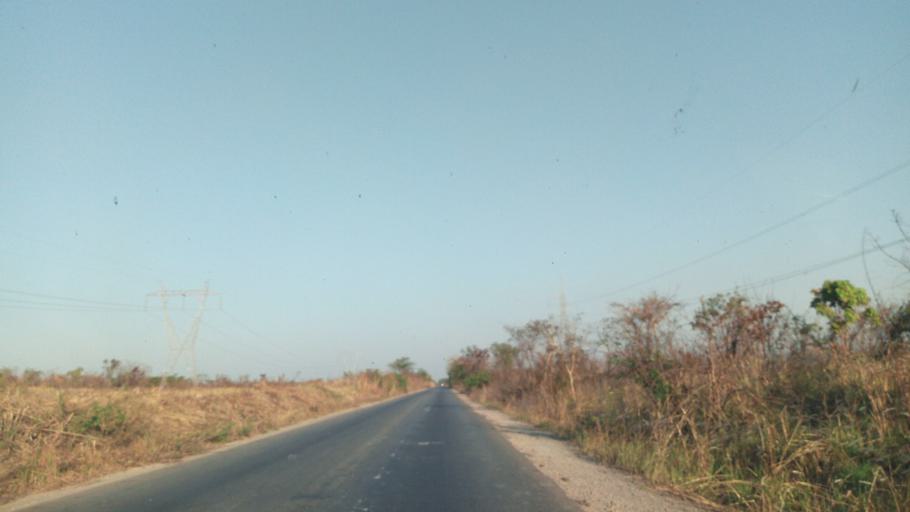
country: CD
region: Katanga
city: Likasi
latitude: -11.1092
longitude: 27.0211
